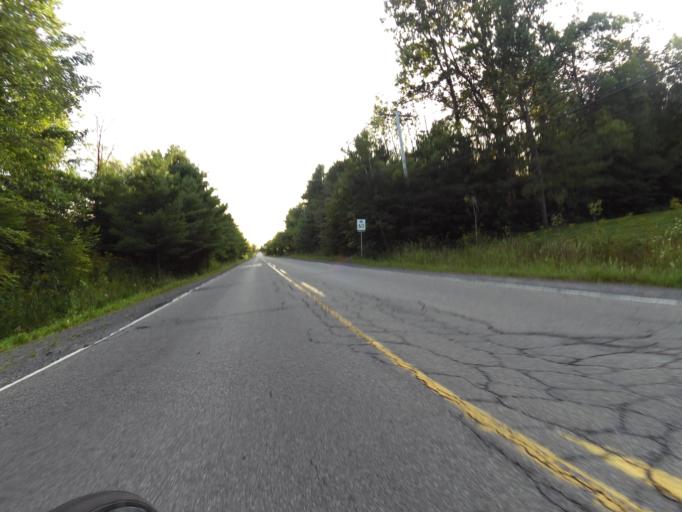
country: CA
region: Ontario
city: Bells Corners
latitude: 45.3798
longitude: -75.9523
